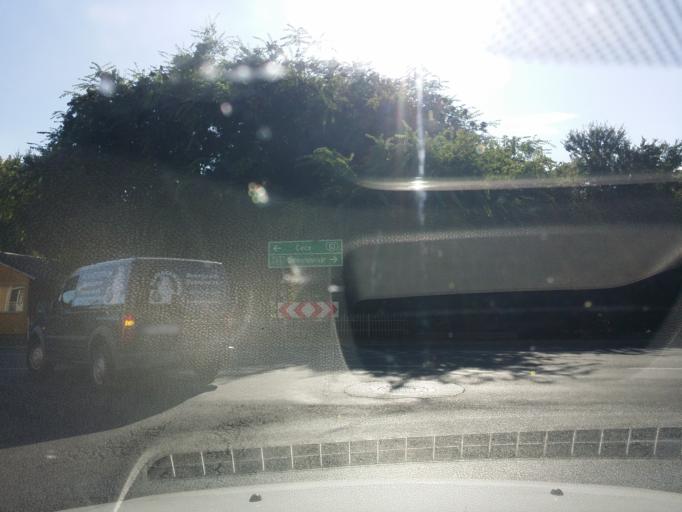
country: HU
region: Fejer
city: Sarbogard
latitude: 46.8589
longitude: 18.6311
